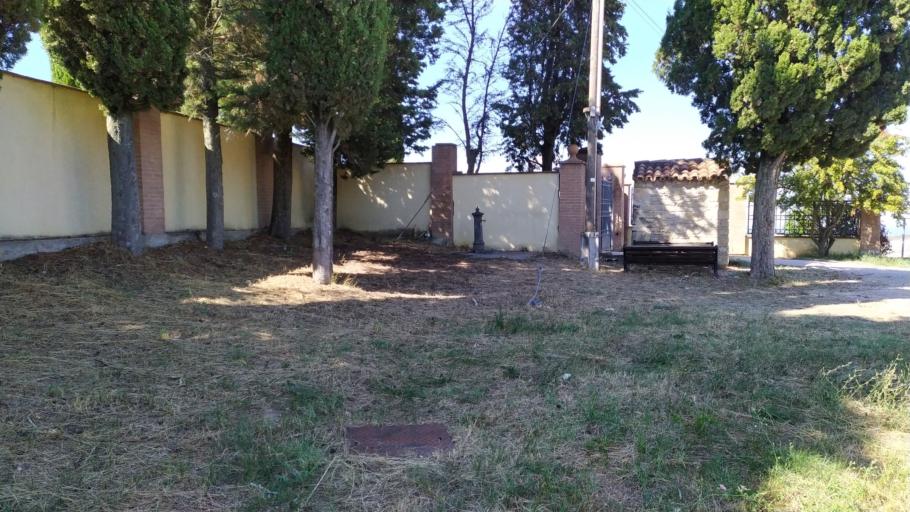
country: IT
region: Emilia-Romagna
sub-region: Forli-Cesena
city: Castrocaro Terme
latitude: 44.1695
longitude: 11.9173
